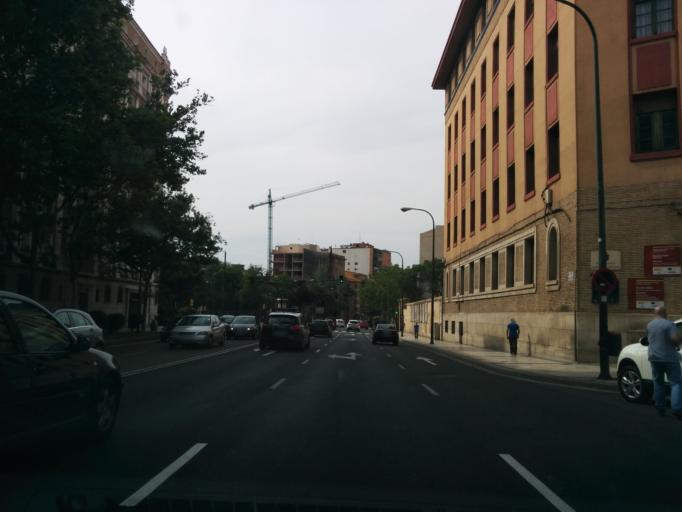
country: ES
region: Aragon
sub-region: Provincia de Zaragoza
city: Almozara
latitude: 41.6530
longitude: -0.8921
